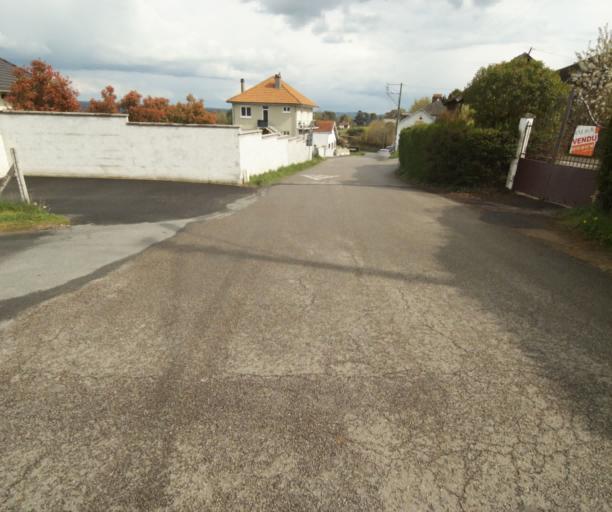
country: FR
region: Limousin
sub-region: Departement de la Correze
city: Tulle
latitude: 45.2743
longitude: 1.7532
